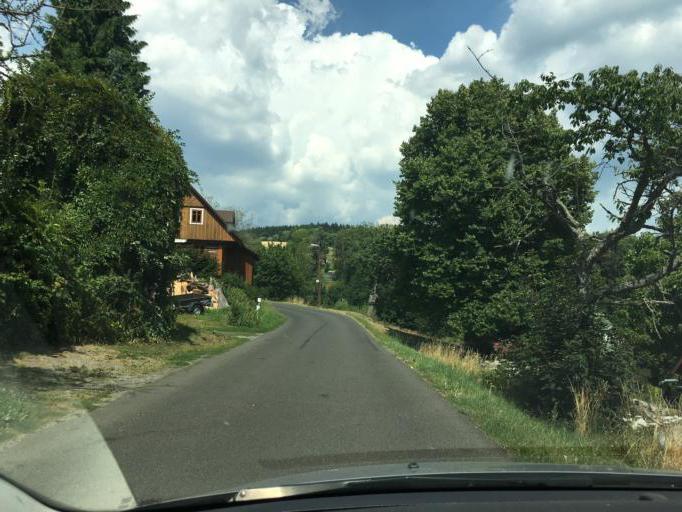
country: CZ
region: Liberecky
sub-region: Okres Semily
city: Ponikla
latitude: 50.6766
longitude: 15.4866
